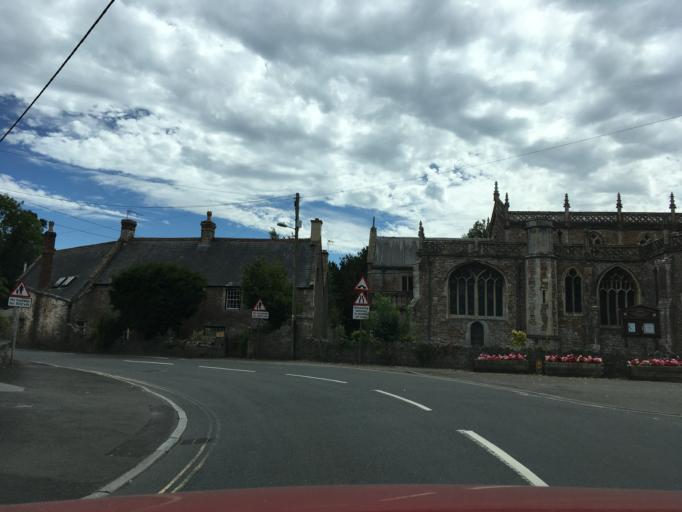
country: GB
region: England
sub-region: Somerset
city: Cheddar
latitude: 51.2741
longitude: -2.7760
